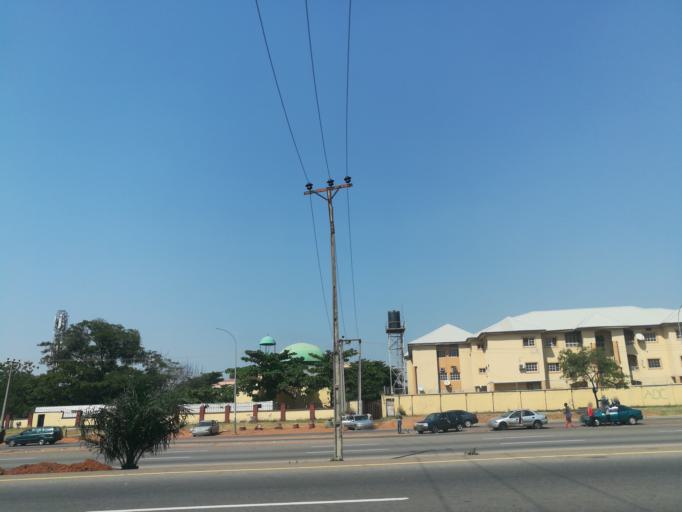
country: NG
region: Abuja Federal Capital Territory
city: Abuja
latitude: 9.0711
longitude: 7.4522
